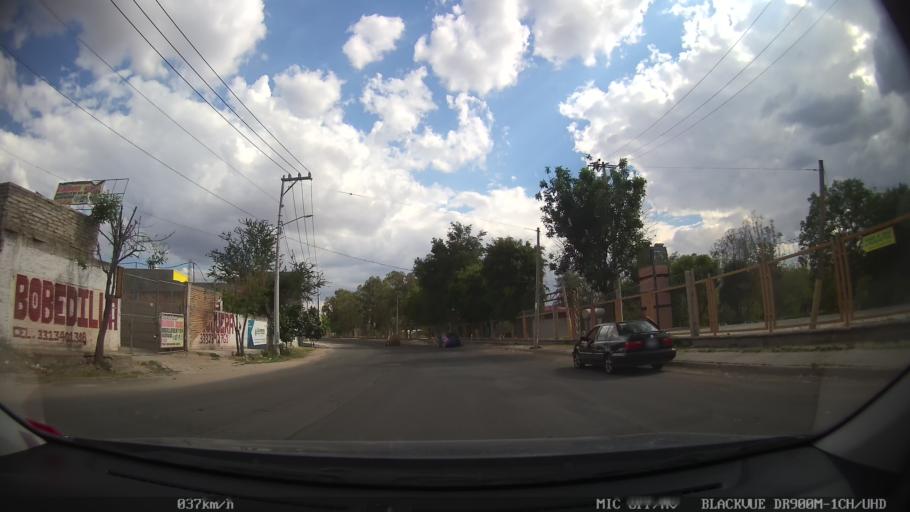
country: MX
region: Jalisco
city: Tlaquepaque
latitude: 20.6654
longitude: -103.2672
